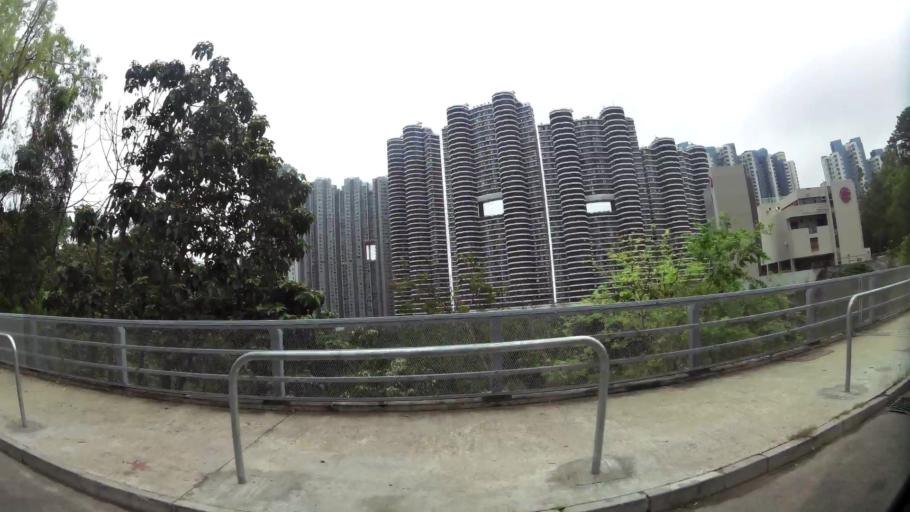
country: HK
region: Central and Western
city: Central
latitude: 22.2556
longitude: 114.1358
